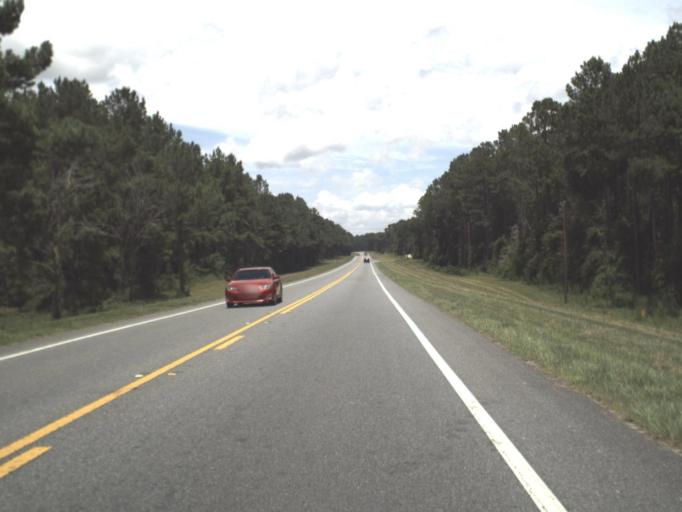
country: US
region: Florida
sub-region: Suwannee County
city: Live Oak
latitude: 30.3427
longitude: -82.9537
